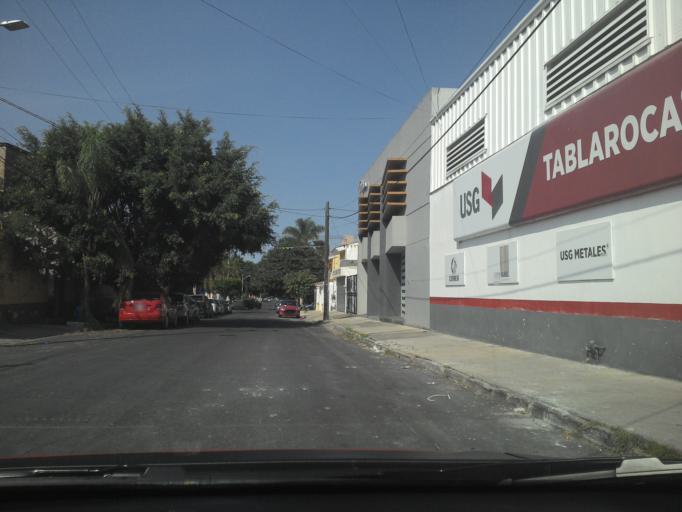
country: MX
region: Jalisco
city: Guadalajara
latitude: 20.6417
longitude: -103.4342
